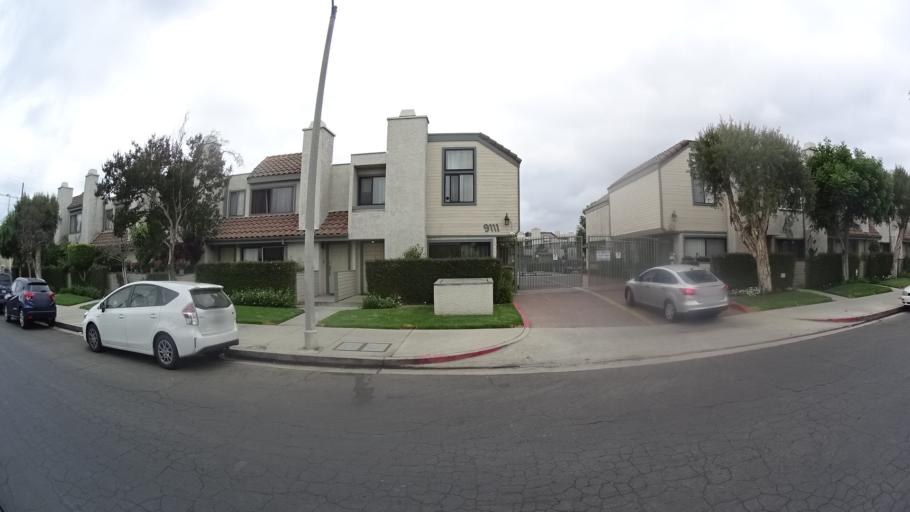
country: US
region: California
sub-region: Los Angeles County
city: San Fernando
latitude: 34.2359
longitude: -118.4589
